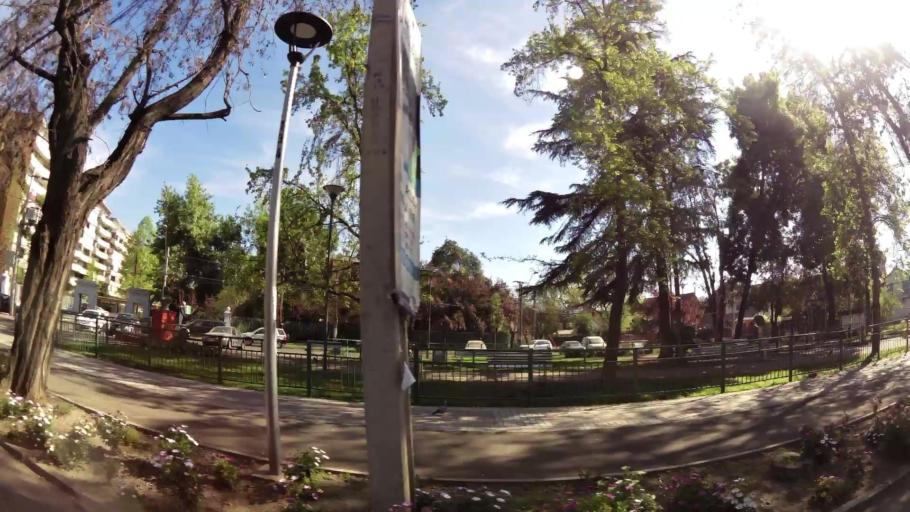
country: CL
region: Santiago Metropolitan
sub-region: Provincia de Santiago
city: Villa Presidente Frei, Nunoa, Santiago, Chile
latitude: -33.4447
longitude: -70.5655
